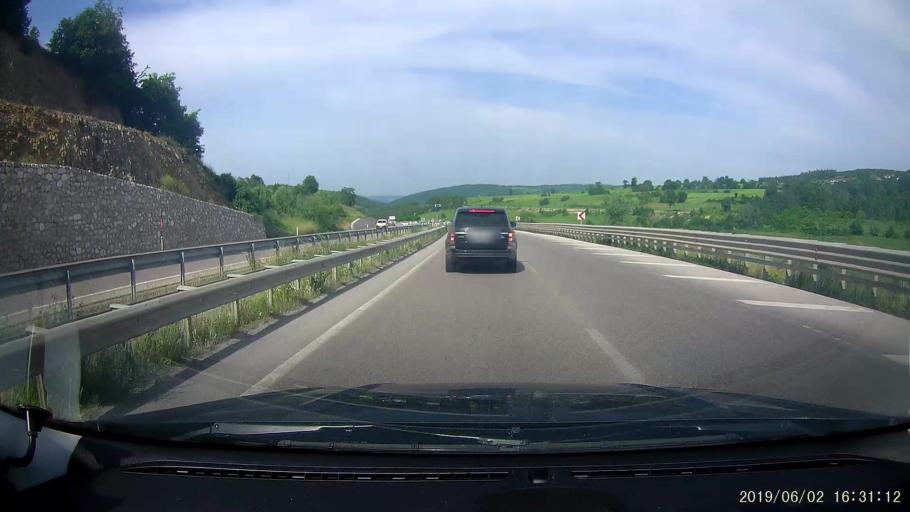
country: TR
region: Samsun
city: Ladik
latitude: 41.0305
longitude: 35.8978
